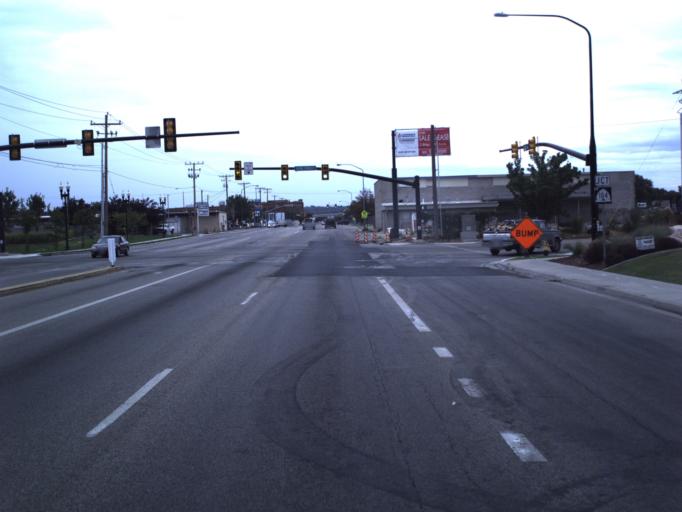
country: US
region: Utah
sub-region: Weber County
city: Ogden
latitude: 41.2318
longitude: -111.9787
